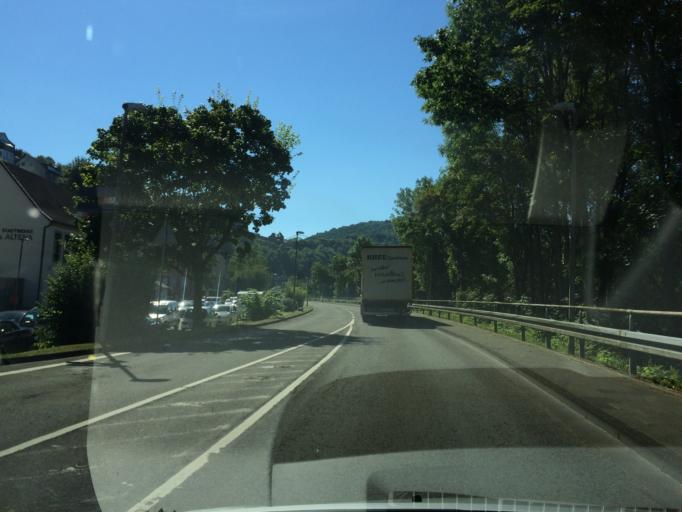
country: DE
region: North Rhine-Westphalia
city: Altena
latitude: 51.3042
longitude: 7.6671
